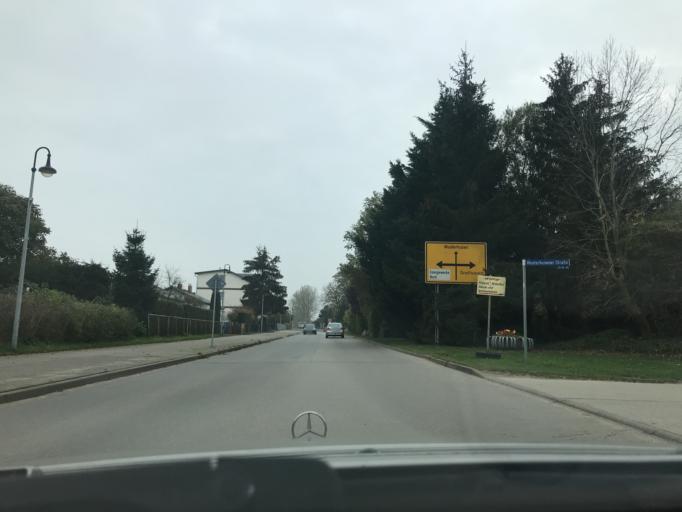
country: DE
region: Mecklenburg-Vorpommern
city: Lubmin
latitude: 54.1292
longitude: 13.6134
